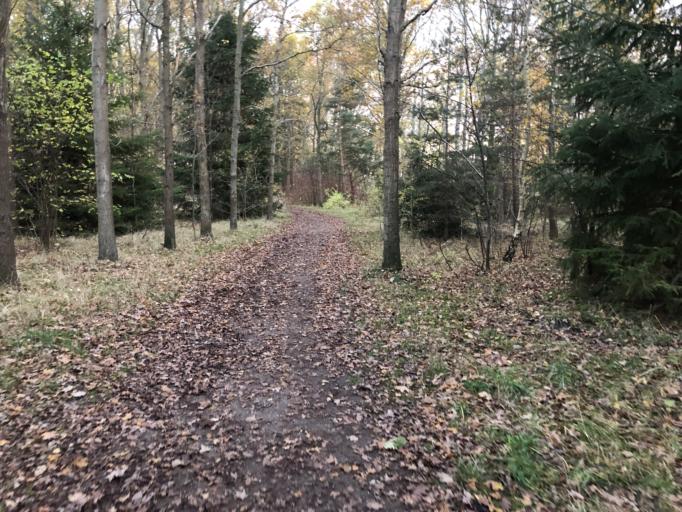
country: DK
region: Capital Region
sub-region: Tarnby Kommune
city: Tarnby
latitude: 55.6040
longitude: 12.5947
